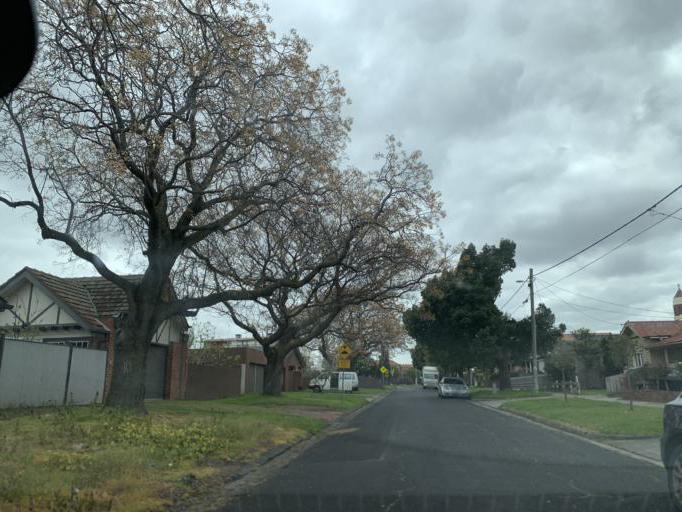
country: AU
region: Victoria
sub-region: Moreland
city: Pascoe Vale South
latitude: -37.7514
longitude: 144.9515
